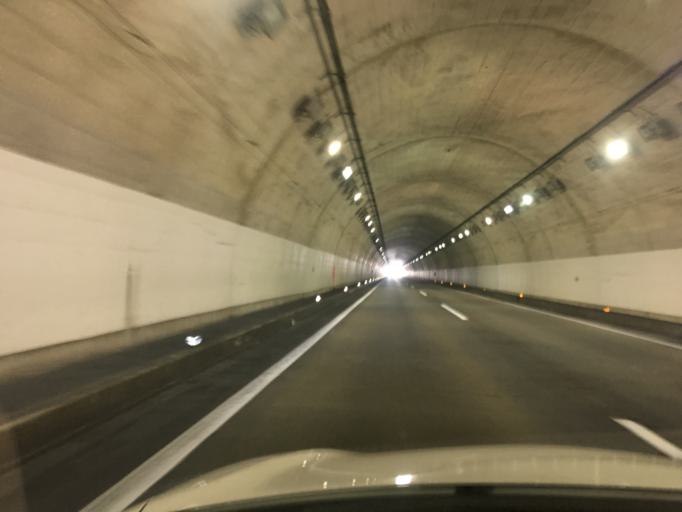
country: JP
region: Fukushima
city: Funehikimachi-funehiki
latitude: 37.3511
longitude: 140.6077
